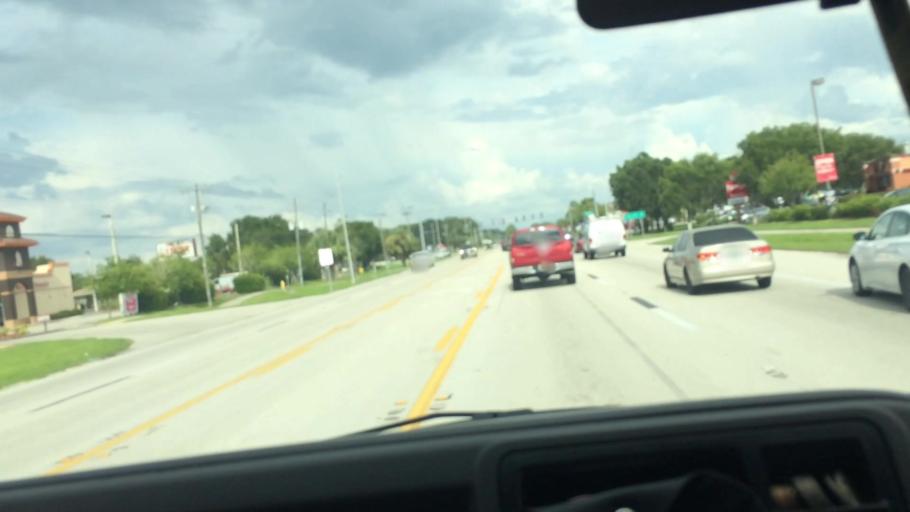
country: US
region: Florida
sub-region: Lee County
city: Olga
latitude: 26.7093
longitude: -81.7231
